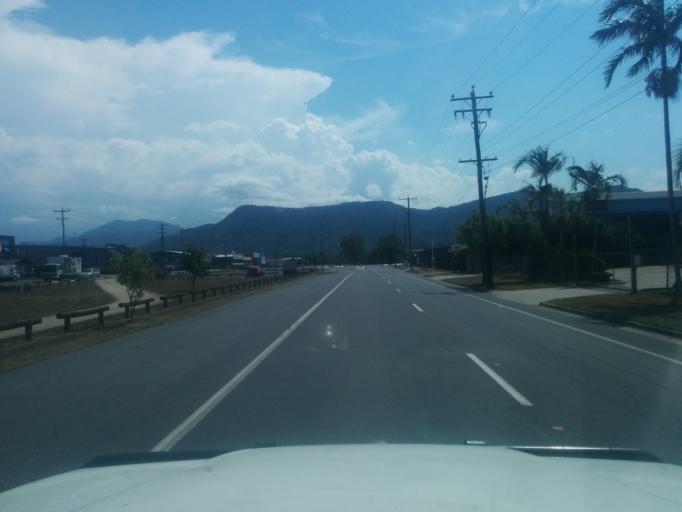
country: AU
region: Queensland
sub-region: Cairns
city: Woree
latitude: -16.9390
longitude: 145.7576
